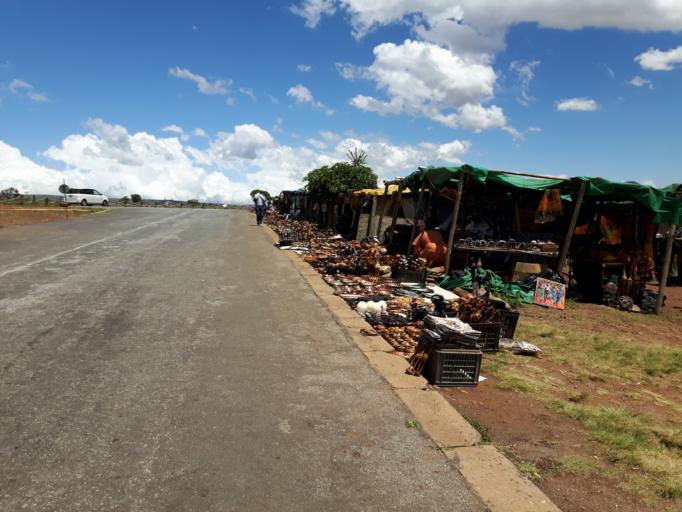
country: ZA
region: Limpopo
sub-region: Mopani District Municipality
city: Hoedspruit
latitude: -24.5741
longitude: 30.7978
